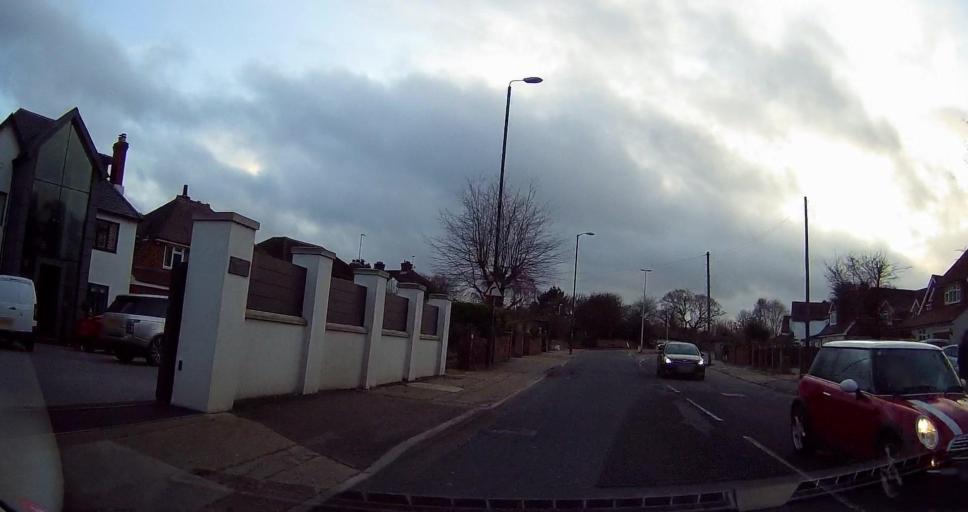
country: GB
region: England
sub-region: Kent
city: Chatham
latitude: 51.3606
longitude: 0.5170
